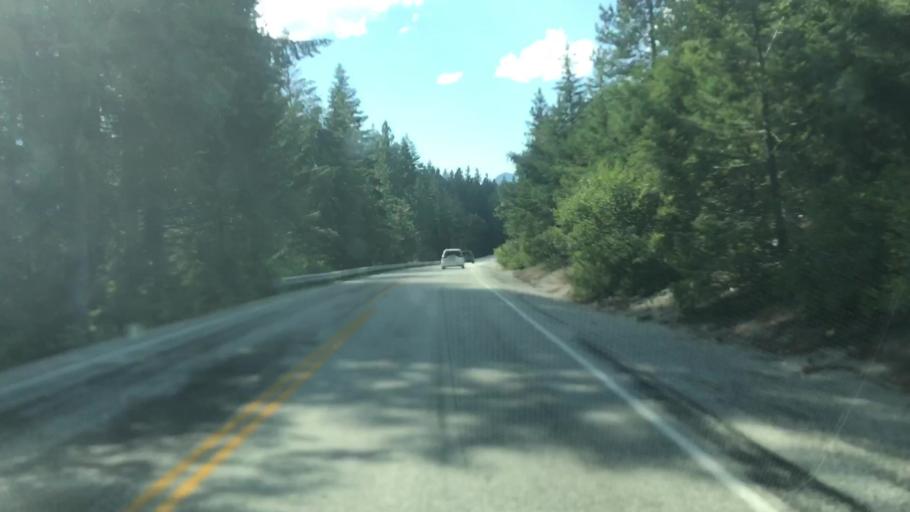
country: US
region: Washington
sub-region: Chelan County
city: Leavenworth
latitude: 47.8207
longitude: -120.7449
